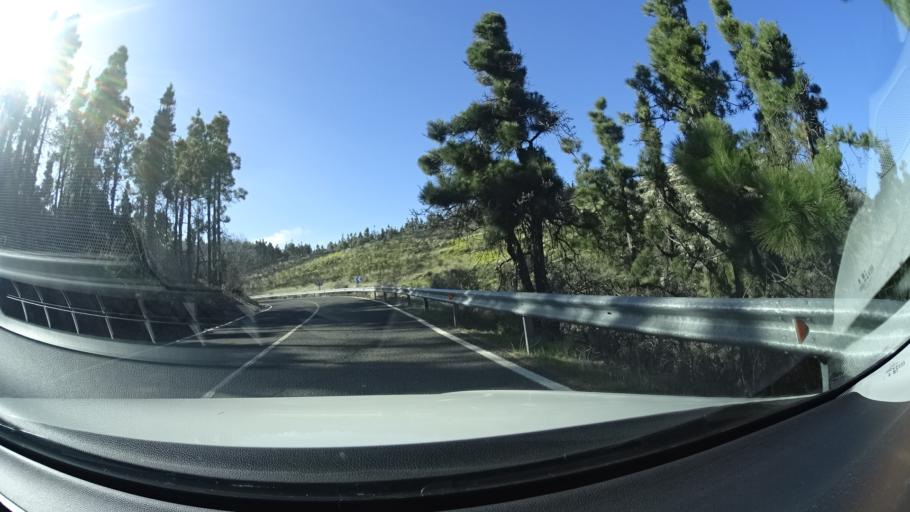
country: ES
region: Canary Islands
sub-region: Provincia de Las Palmas
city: San Bartolome
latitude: 27.9651
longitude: -15.5570
